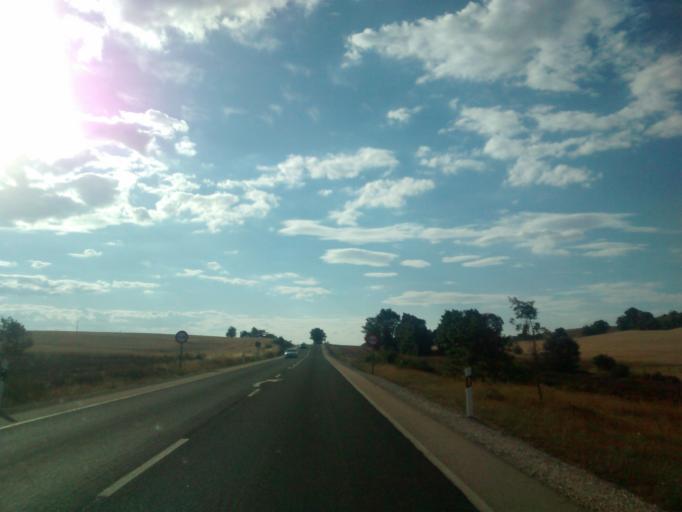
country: ES
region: Castille and Leon
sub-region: Provincia de Burgos
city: Basconcillos del Tozo
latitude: 42.6698
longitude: -3.9275
